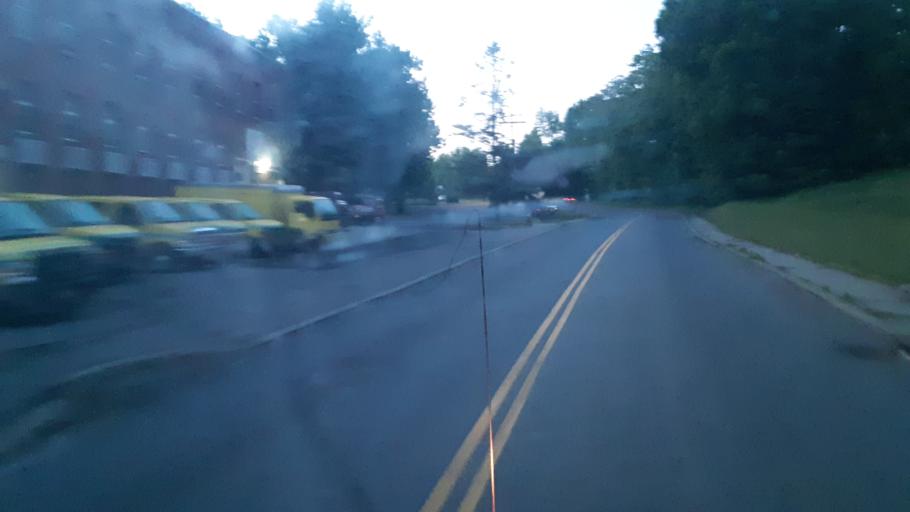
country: US
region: New York
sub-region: Montgomery County
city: Amsterdam
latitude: 42.9396
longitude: -74.1852
